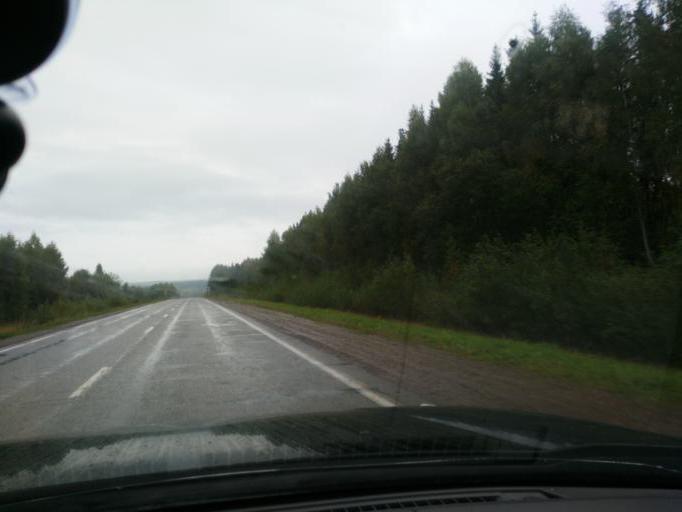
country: RU
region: Perm
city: Osa
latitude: 57.4421
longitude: 55.6362
